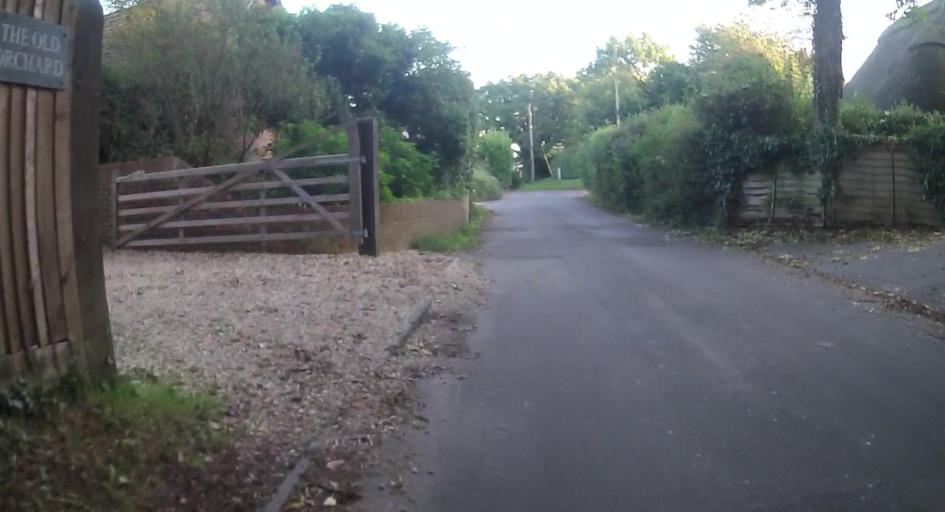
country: GB
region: England
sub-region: Hampshire
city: Old Basing
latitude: 51.2597
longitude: -1.0205
